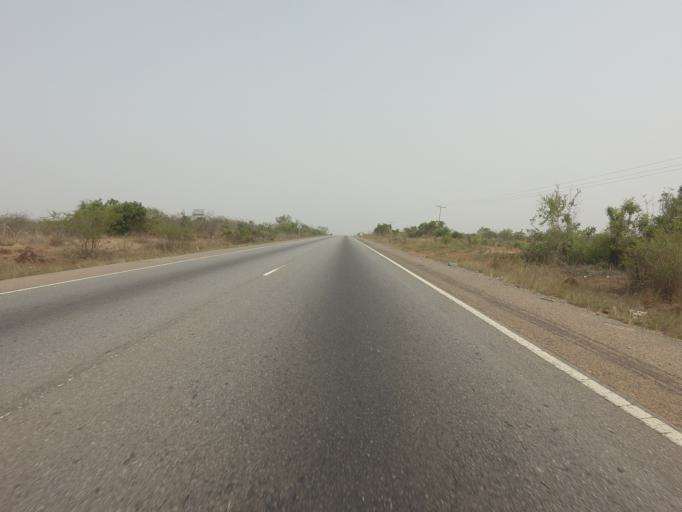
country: GH
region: Greater Accra
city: Tema
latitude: 5.8692
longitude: 0.3155
